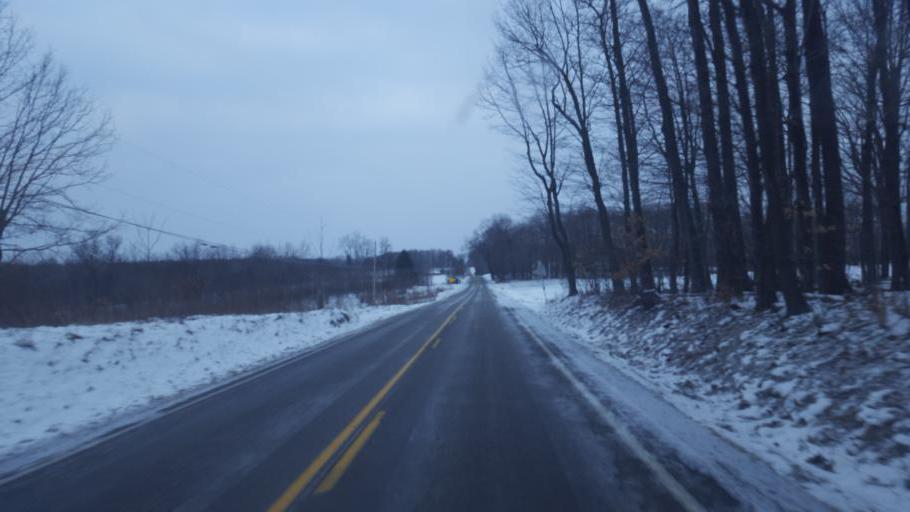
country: US
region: Pennsylvania
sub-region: Mercer County
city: Stoneboro
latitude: 41.4041
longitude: -80.0055
